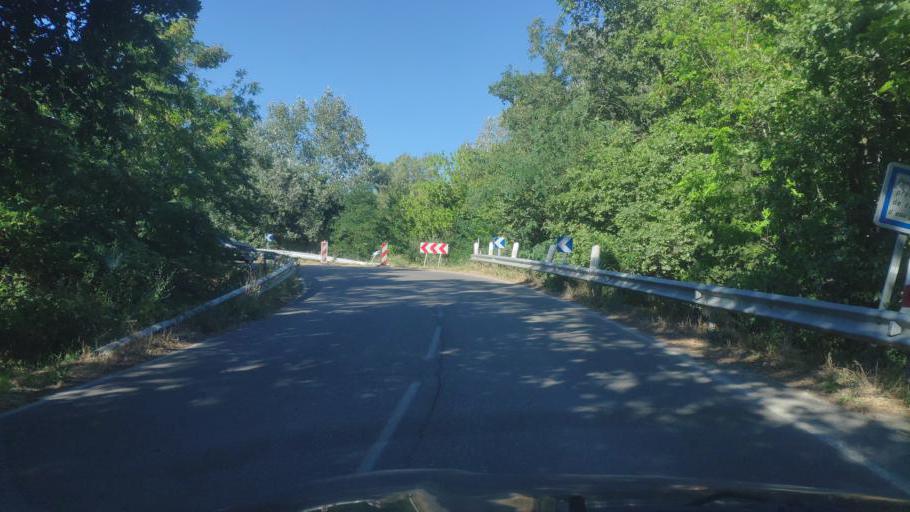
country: FR
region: Provence-Alpes-Cote d'Azur
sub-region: Departement du Vaucluse
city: Aubignan
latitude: 44.0868
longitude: 5.0204
